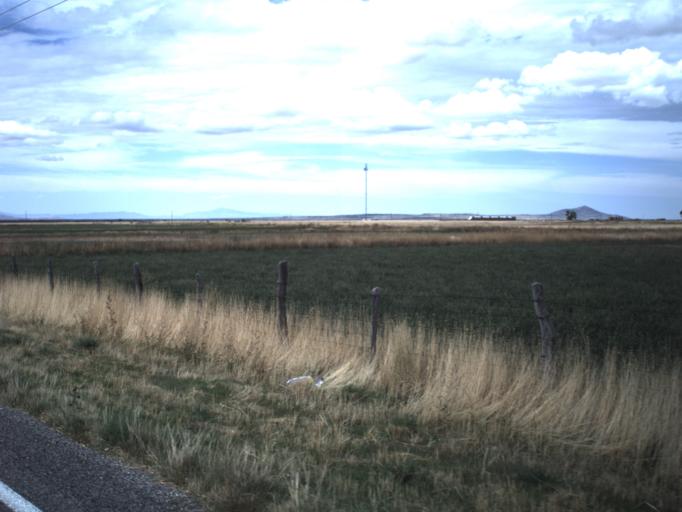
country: US
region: Utah
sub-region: Millard County
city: Fillmore
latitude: 38.9792
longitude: -112.4023
